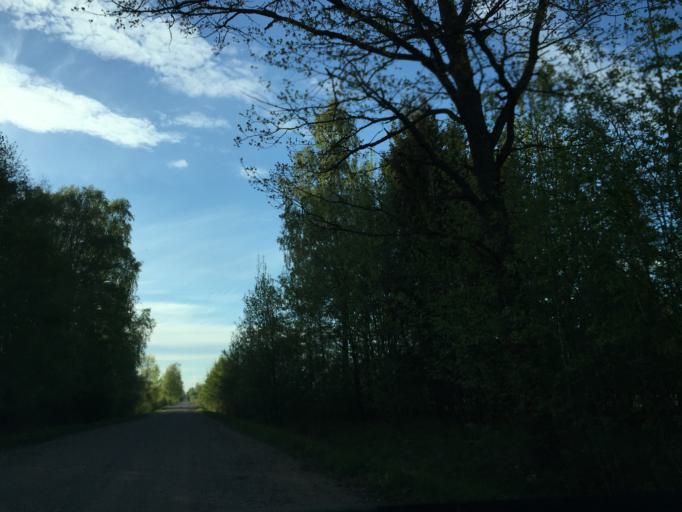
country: LV
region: Saulkrastu
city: Saulkrasti
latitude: 57.4090
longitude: 24.5382
